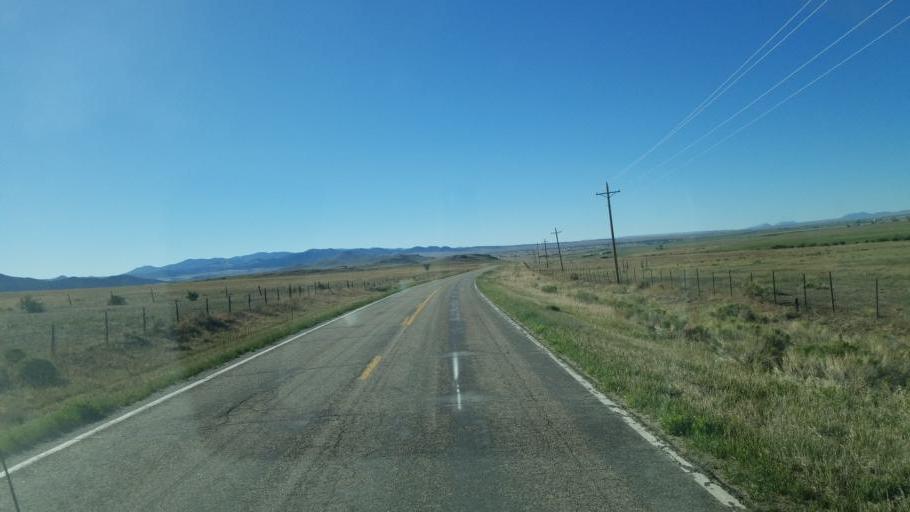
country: US
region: Colorado
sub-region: Custer County
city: Westcliffe
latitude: 38.1894
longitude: -105.5180
